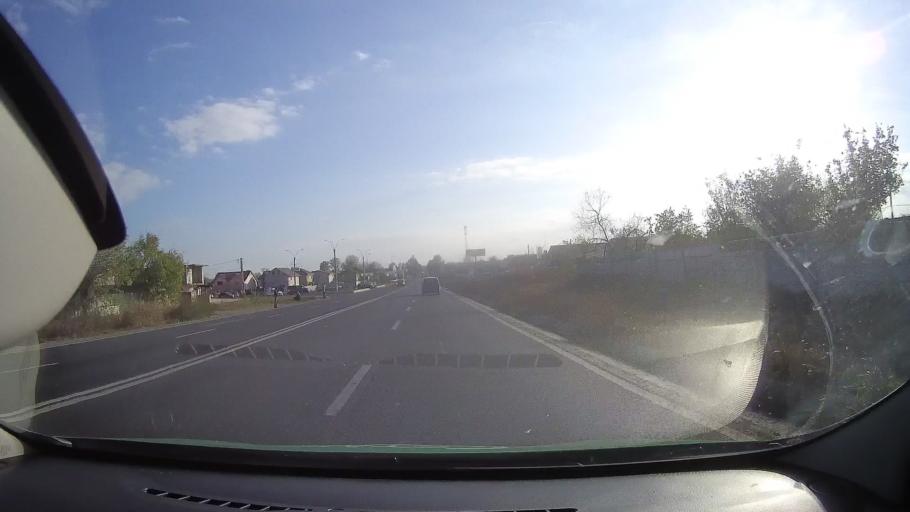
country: RO
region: Constanta
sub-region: Comuna Lumina
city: Lumina
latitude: 44.2855
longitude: 28.5567
